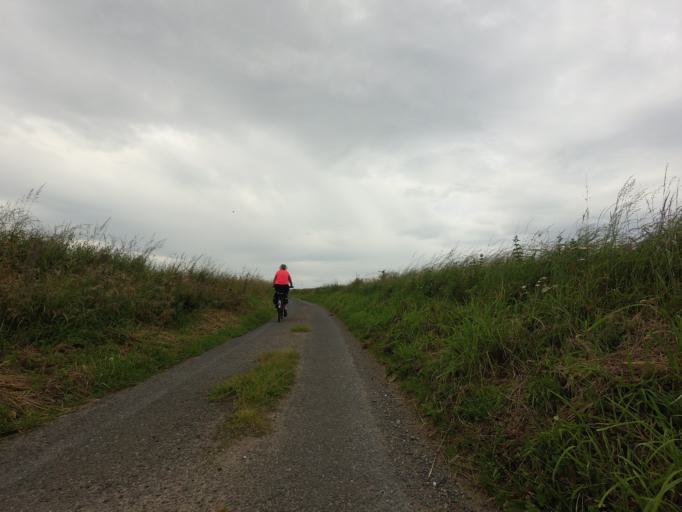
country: GB
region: Scotland
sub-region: Aberdeenshire
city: Whitehills
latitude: 57.6765
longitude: -2.5957
